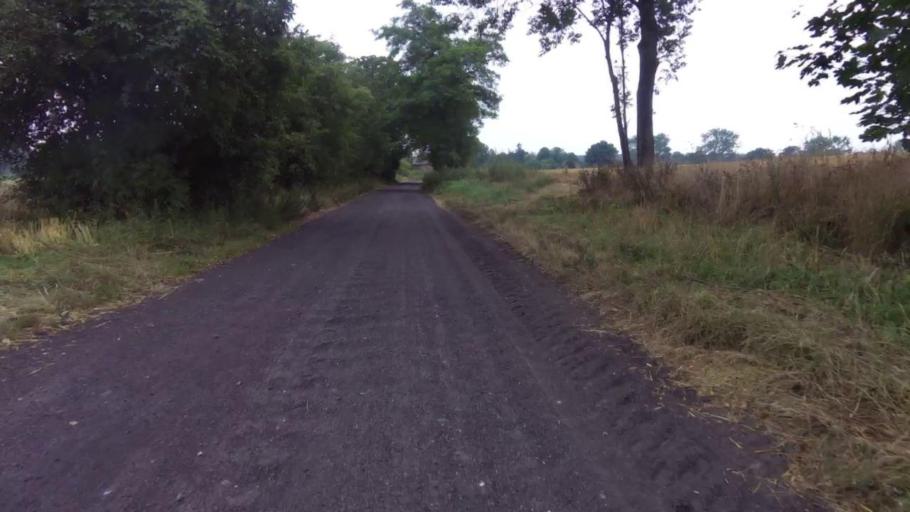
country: PL
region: West Pomeranian Voivodeship
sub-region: Powiat choszczenski
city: Choszczno
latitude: 53.2322
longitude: 15.3827
